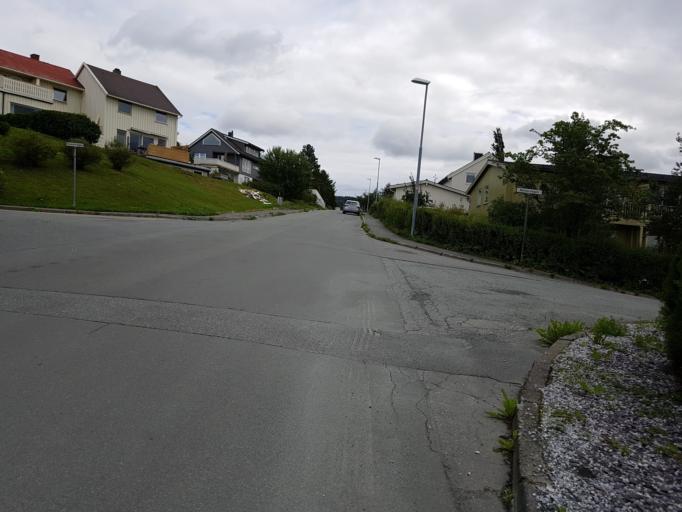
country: NO
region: Sor-Trondelag
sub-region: Trondheim
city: Trondheim
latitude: 63.3952
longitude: 10.4182
